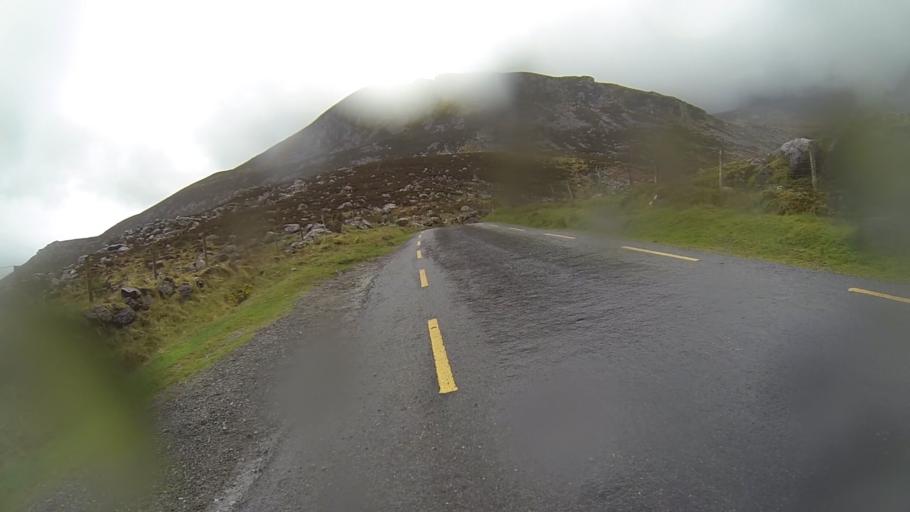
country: IE
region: Munster
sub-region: Ciarrai
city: Cill Airne
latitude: 52.0313
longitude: -9.6364
